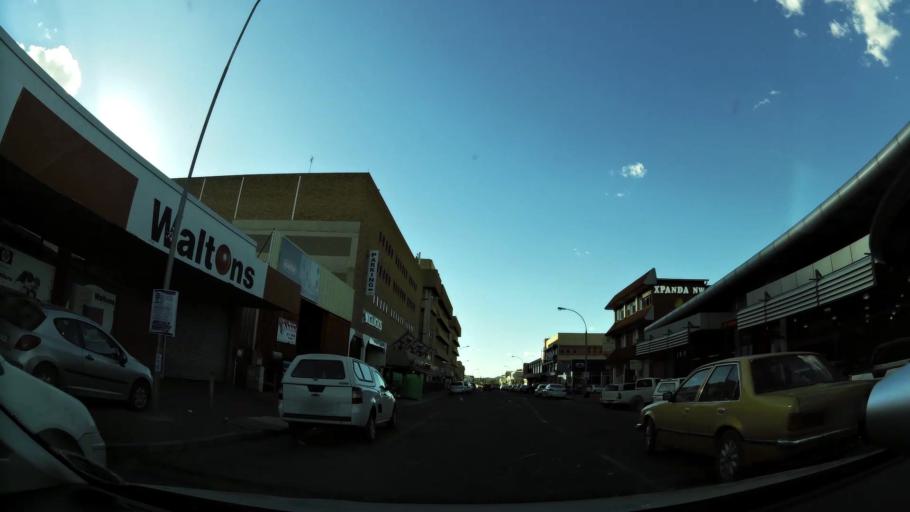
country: ZA
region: North-West
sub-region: Dr Kenneth Kaunda District Municipality
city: Klerksdorp
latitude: -26.8693
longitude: 26.6676
